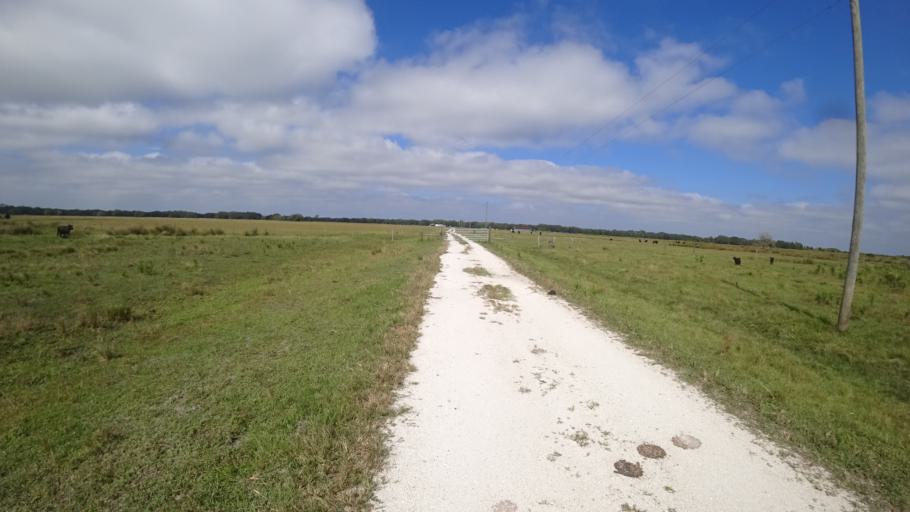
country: US
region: Florida
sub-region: DeSoto County
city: Arcadia
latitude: 27.3240
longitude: -82.1101
